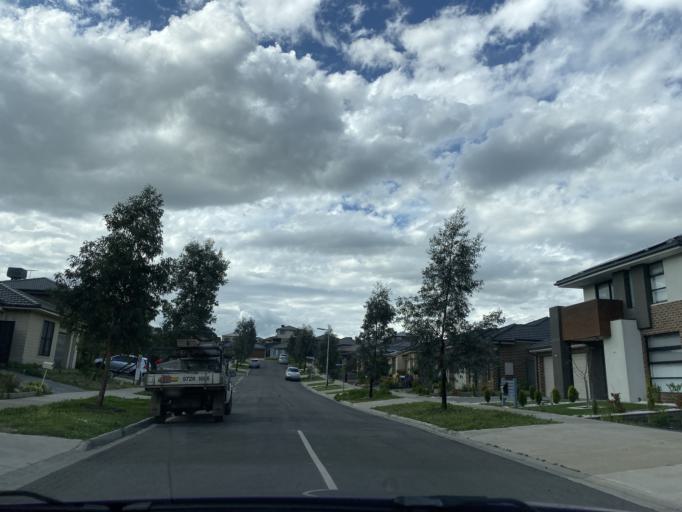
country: AU
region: Victoria
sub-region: Whittlesea
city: Mernda
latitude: -37.5982
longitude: 145.0789
